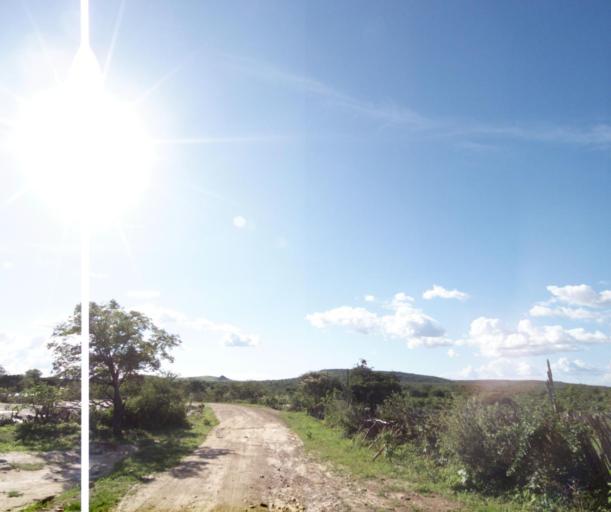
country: BR
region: Bahia
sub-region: Tanhacu
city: Tanhacu
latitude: -14.1868
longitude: -40.9487
